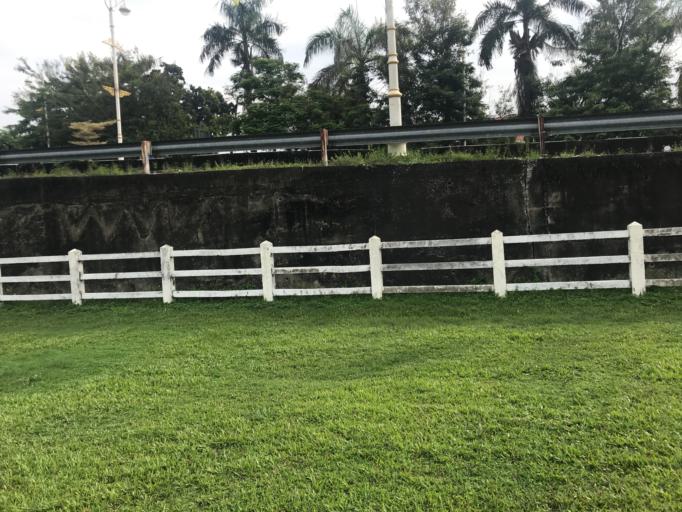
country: MY
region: Perak
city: Ipoh
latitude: 4.5999
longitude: 101.0764
